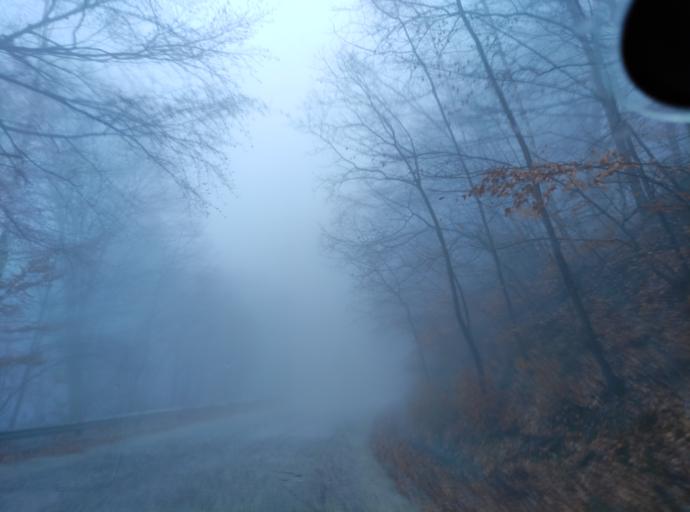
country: BG
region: Sofia-Capital
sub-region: Stolichna Obshtina
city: Sofia
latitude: 42.6203
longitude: 23.2959
